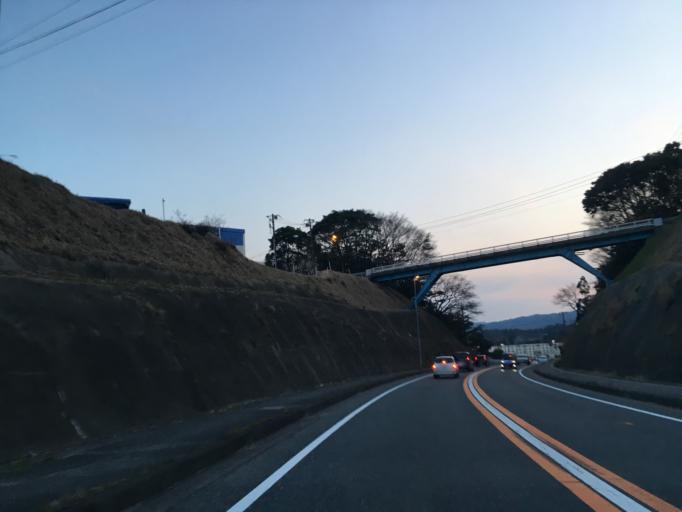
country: JP
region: Ibaraki
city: Takahagi
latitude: 36.7356
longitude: 140.7239
